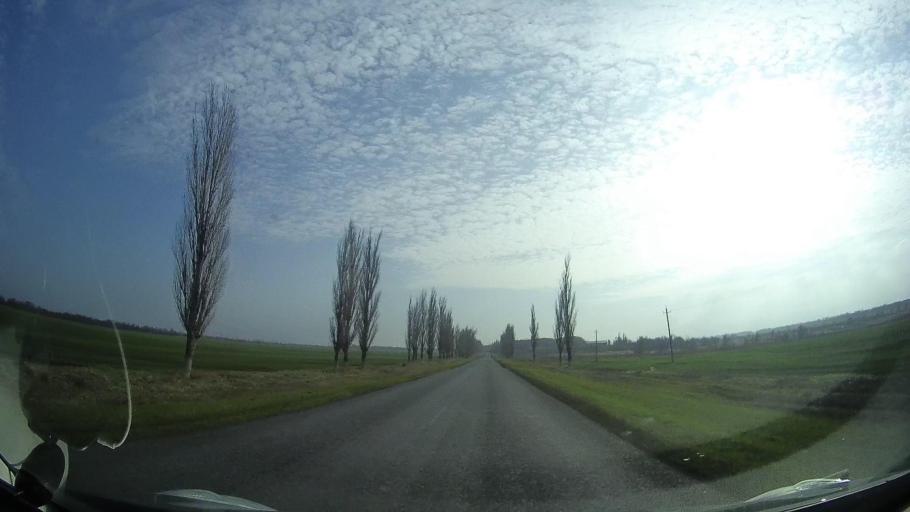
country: RU
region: Rostov
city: Mechetinskaya
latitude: 46.8325
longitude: 40.5503
